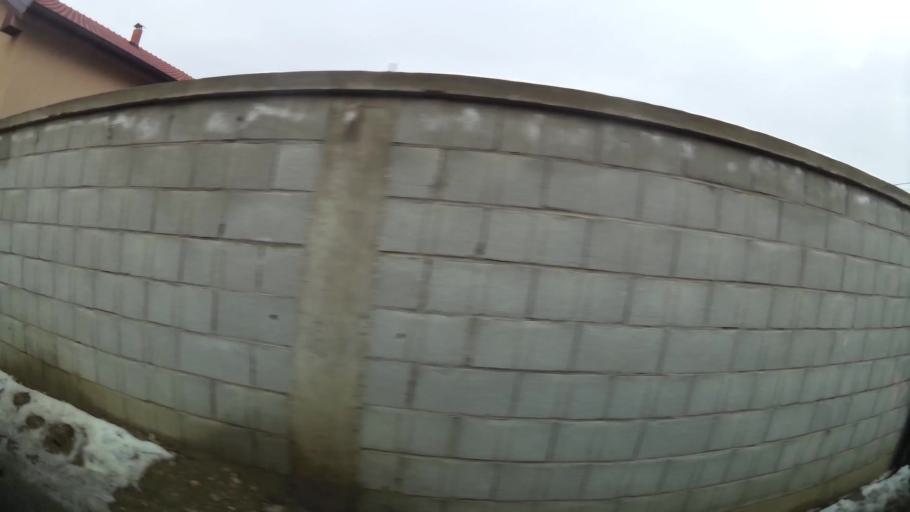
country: MK
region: Suto Orizari
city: Suto Orizare
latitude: 42.0352
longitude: 21.4164
